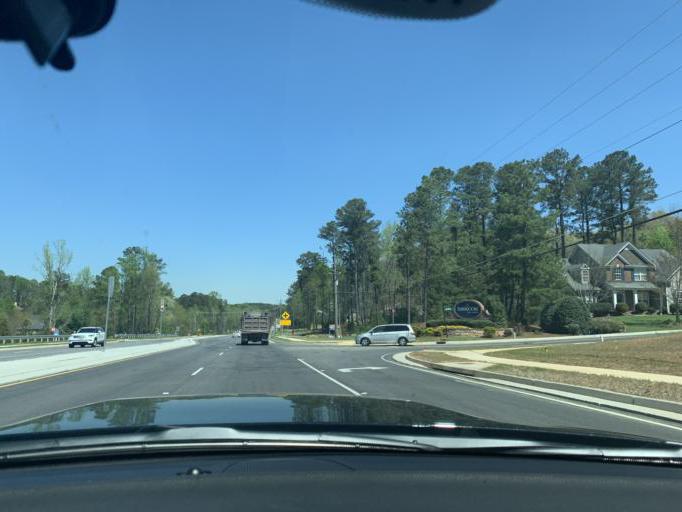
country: US
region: Georgia
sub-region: Forsyth County
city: Cumming
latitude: 34.2043
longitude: -84.1973
